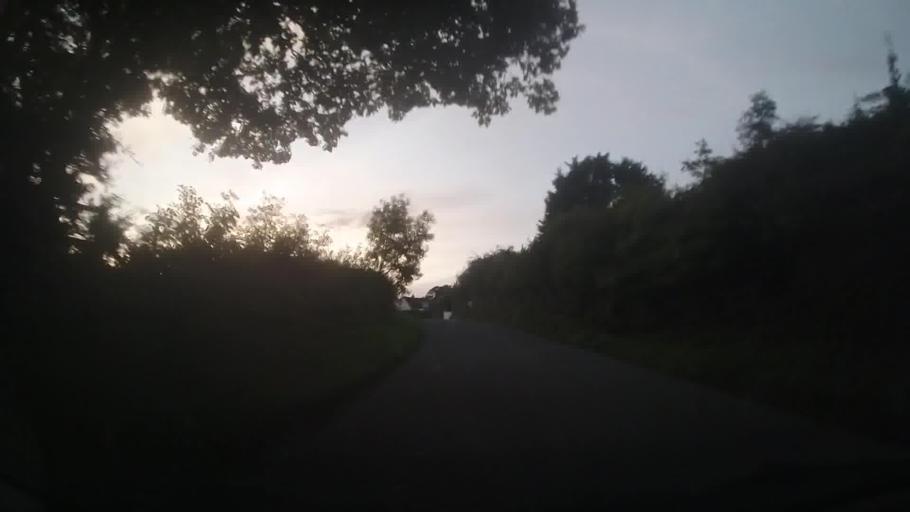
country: GB
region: Wales
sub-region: Pembrokeshire
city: Saundersfoot
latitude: 51.7343
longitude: -4.6740
